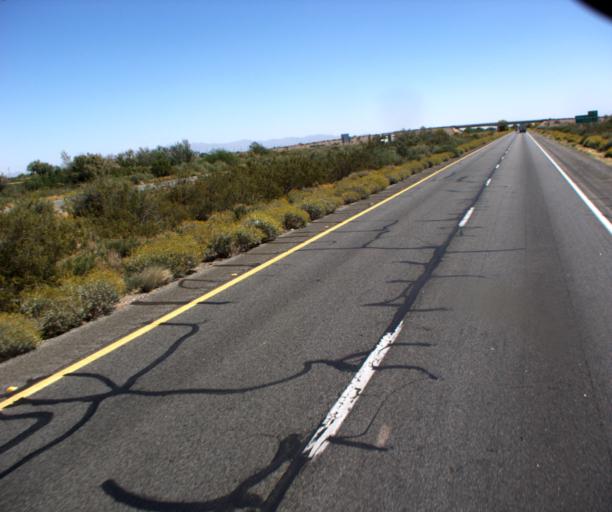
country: US
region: Arizona
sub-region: Maricopa County
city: Buckeye
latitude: 33.4908
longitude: -112.9081
